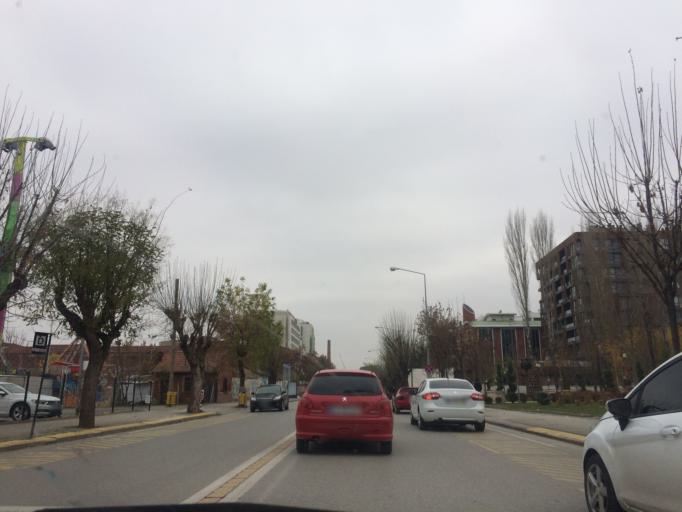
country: TR
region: Eskisehir
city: Eskisehir
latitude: 39.7842
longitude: 30.5032
